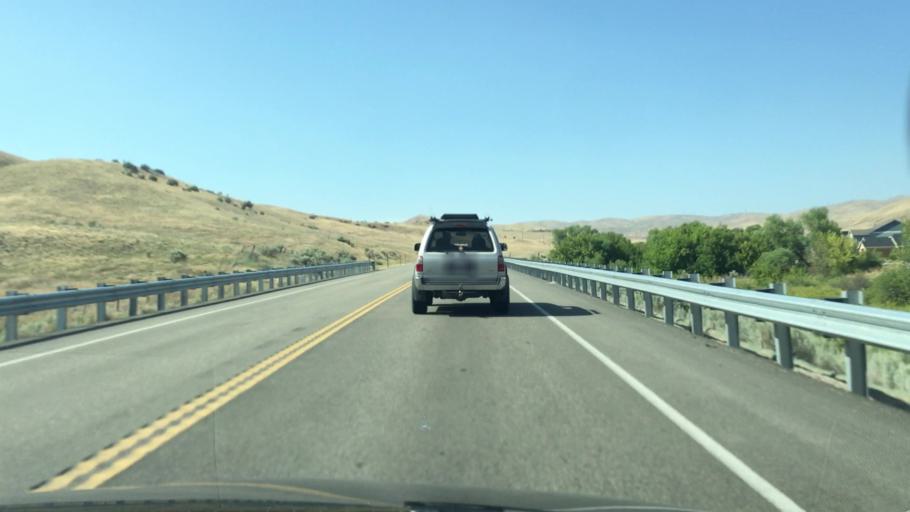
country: US
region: Idaho
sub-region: Ada County
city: Eagle
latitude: 43.7660
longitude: -116.2658
